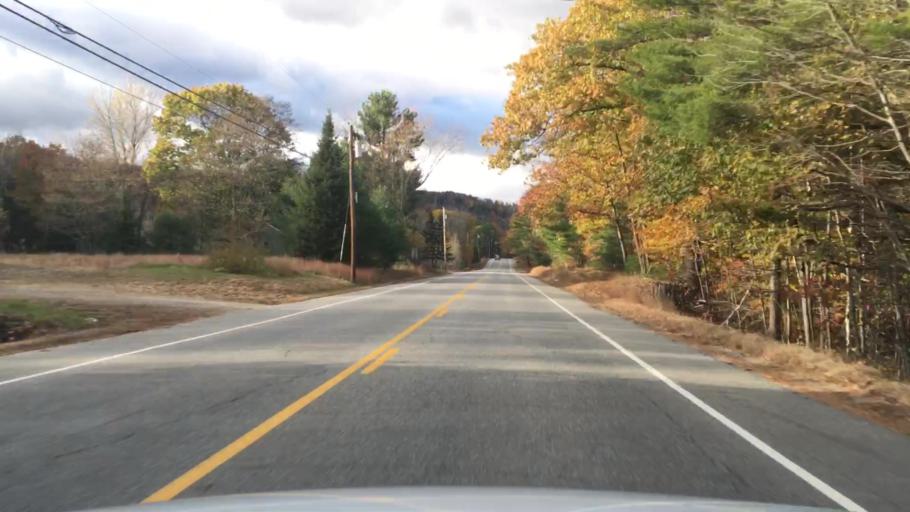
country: US
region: Maine
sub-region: Androscoggin County
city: Livermore
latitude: 44.3795
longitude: -70.2510
